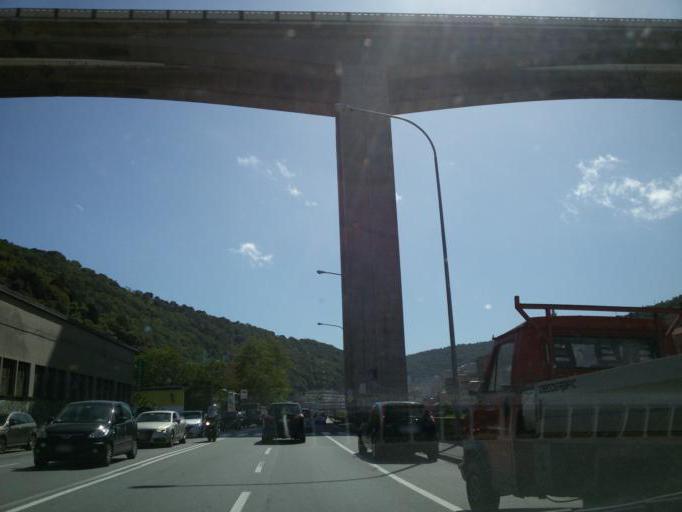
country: IT
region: Liguria
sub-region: Provincia di Genova
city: Genoa
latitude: 44.4335
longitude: 8.9616
